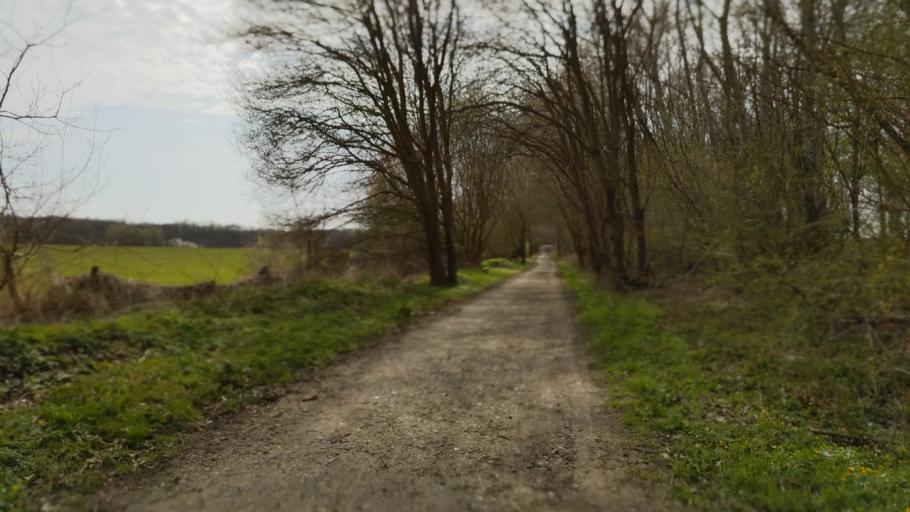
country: DE
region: Schleswig-Holstein
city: Travemuende
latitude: 53.9649
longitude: 10.9355
